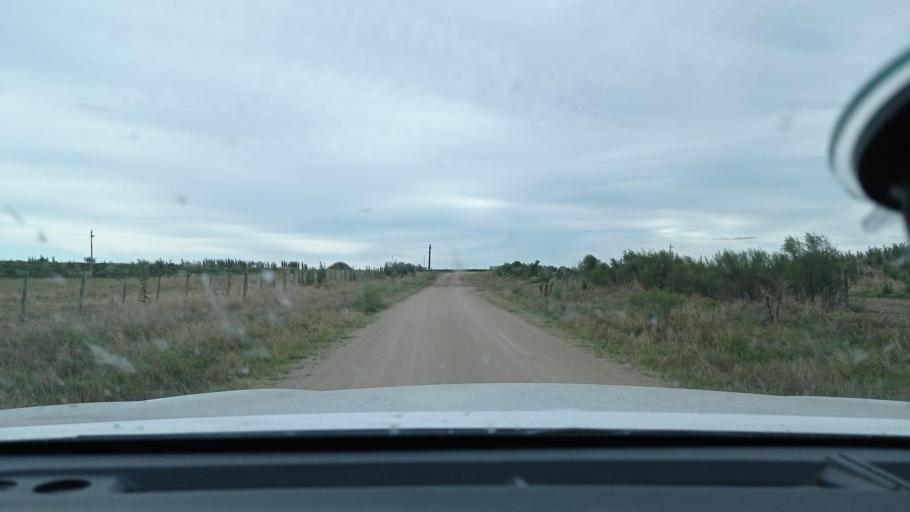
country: UY
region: Florida
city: Casupa
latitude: -34.1050
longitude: -55.7549
